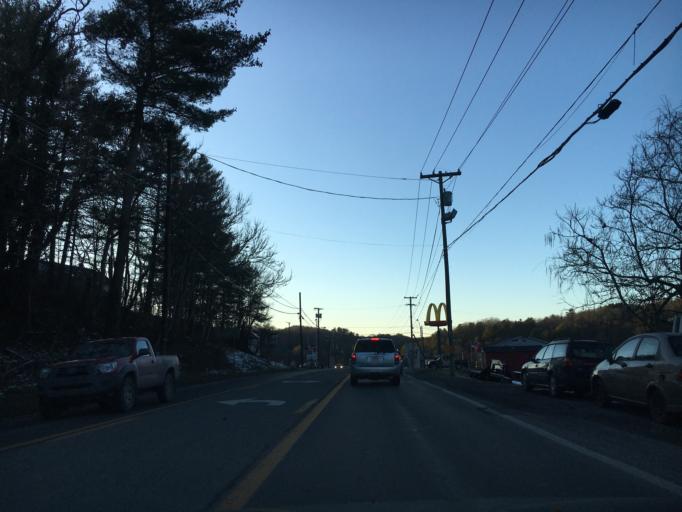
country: US
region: West Virginia
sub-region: Raleigh County
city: Daniels
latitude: 37.7487
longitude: -81.1329
